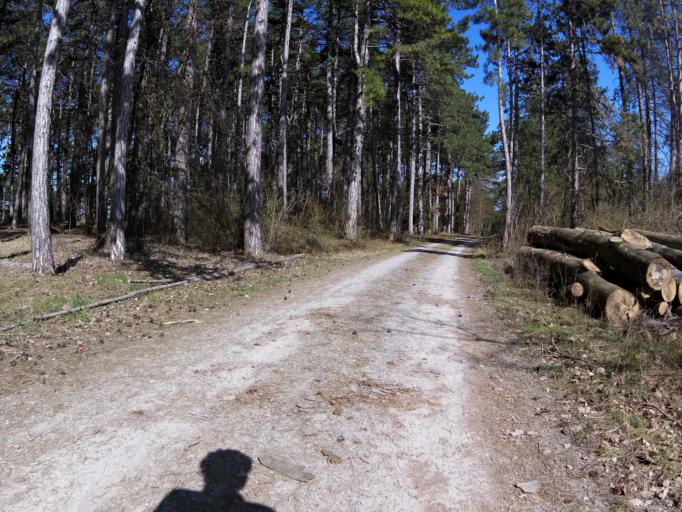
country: DE
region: Bavaria
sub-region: Regierungsbezirk Unterfranken
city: Erlabrunn
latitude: 49.8521
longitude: 9.8133
